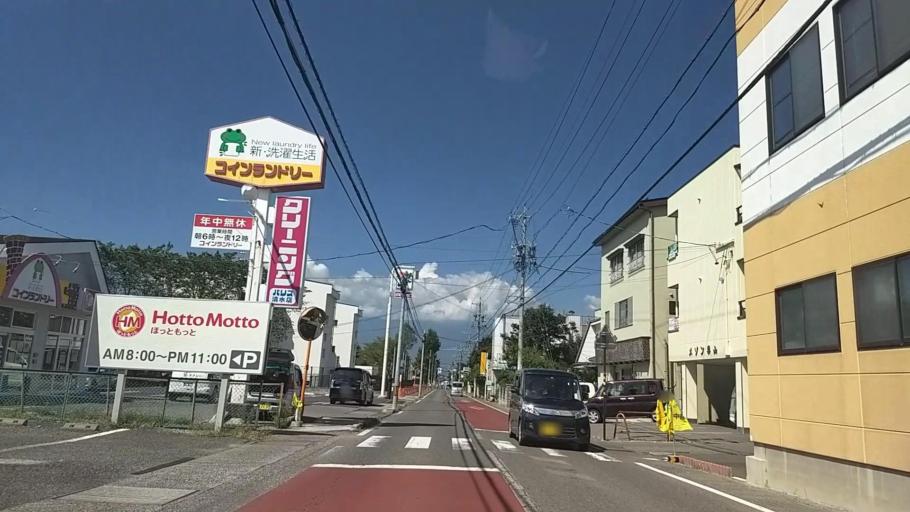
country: JP
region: Nagano
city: Matsumoto
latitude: 36.2373
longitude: 137.9862
